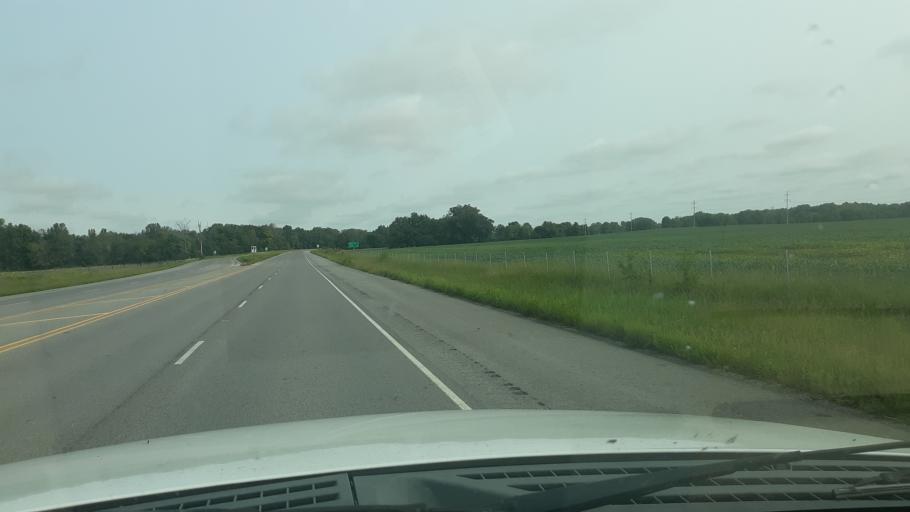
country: US
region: Illinois
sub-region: Saline County
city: Eldorado
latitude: 37.8165
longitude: -88.4268
